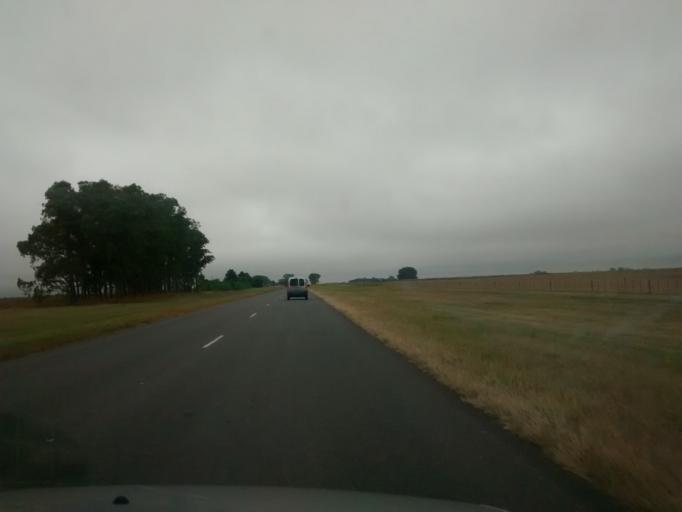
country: AR
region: Buenos Aires
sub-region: Partido de Ayacucho
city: Ayacucho
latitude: -37.2391
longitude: -58.4911
